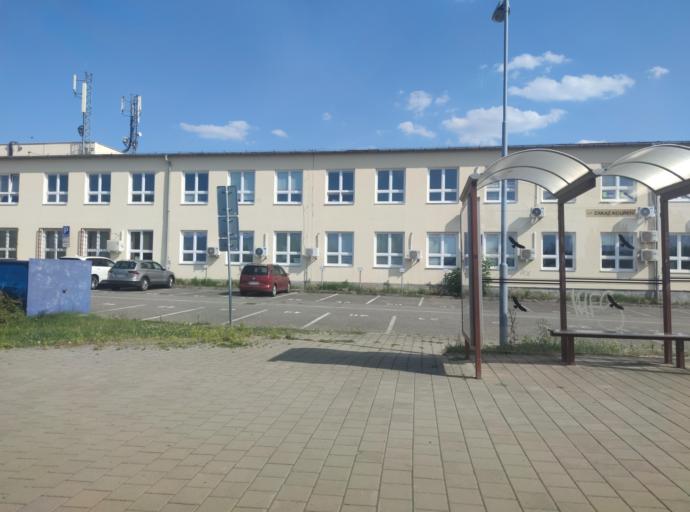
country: CZ
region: South Moravian
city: Podoli
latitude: 49.1725
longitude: 16.6821
